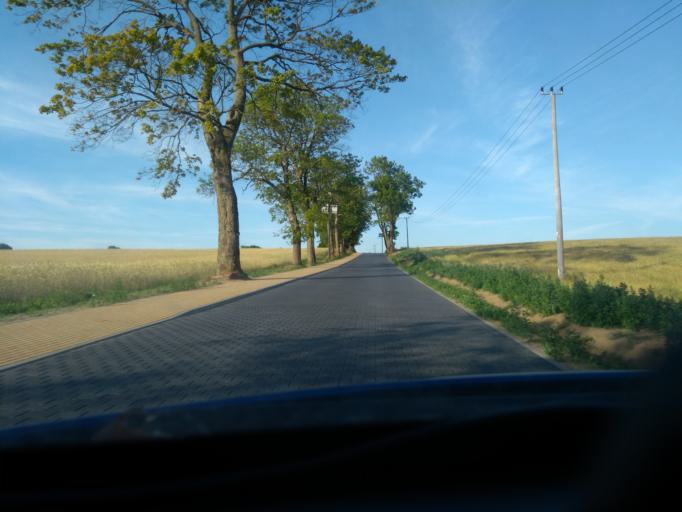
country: PL
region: Pomeranian Voivodeship
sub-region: Powiat kartuski
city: Przodkowo
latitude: 54.3932
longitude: 18.3242
